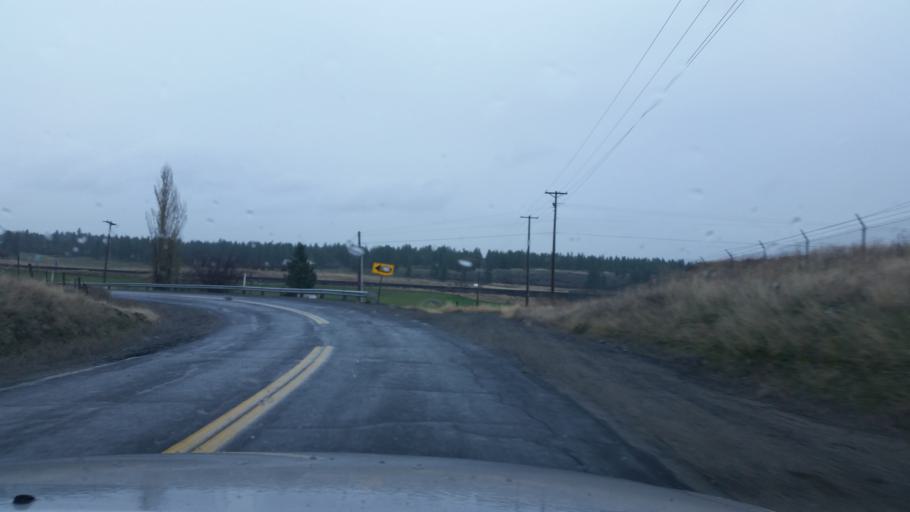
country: US
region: Washington
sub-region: Spokane County
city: Airway Heights
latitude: 47.6856
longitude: -117.5611
